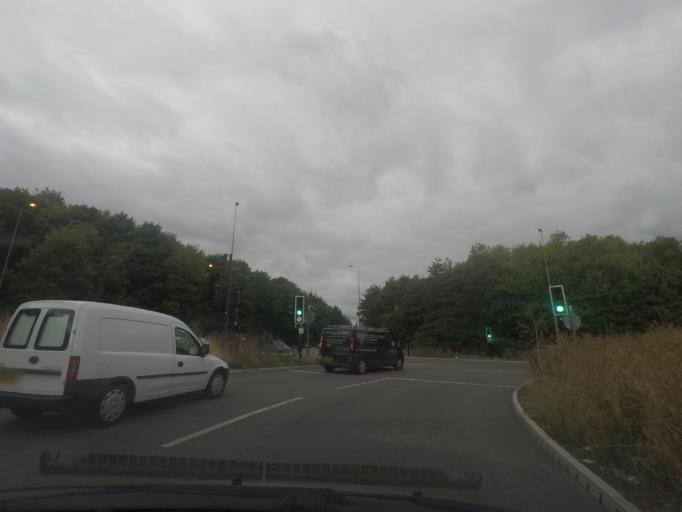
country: GB
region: England
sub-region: Oxfordshire
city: Harwell
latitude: 51.6184
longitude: -1.3035
